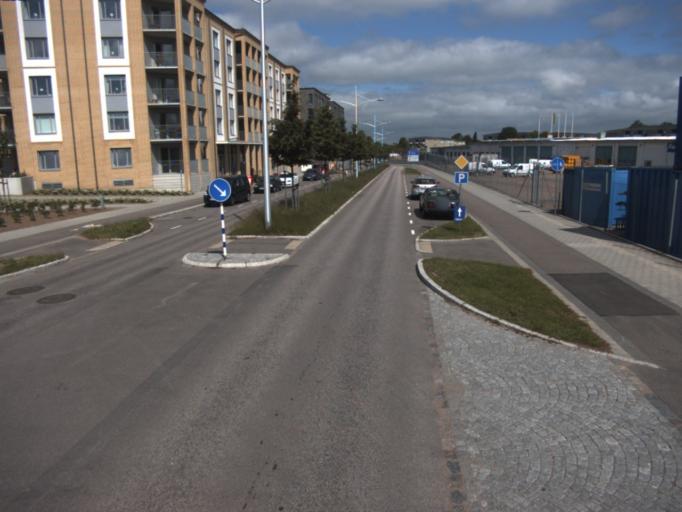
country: SE
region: Skane
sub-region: Helsingborg
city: Helsingborg
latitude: 56.0660
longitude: 12.7073
